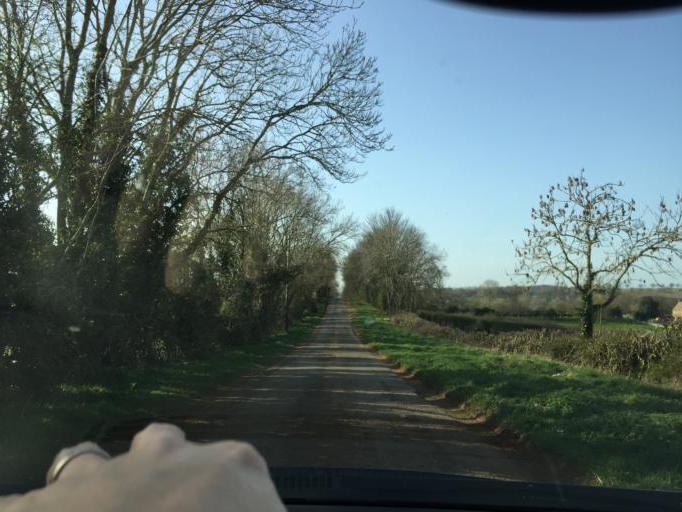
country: GB
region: England
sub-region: Oxfordshire
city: Bloxham
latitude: 52.0332
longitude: -1.3886
